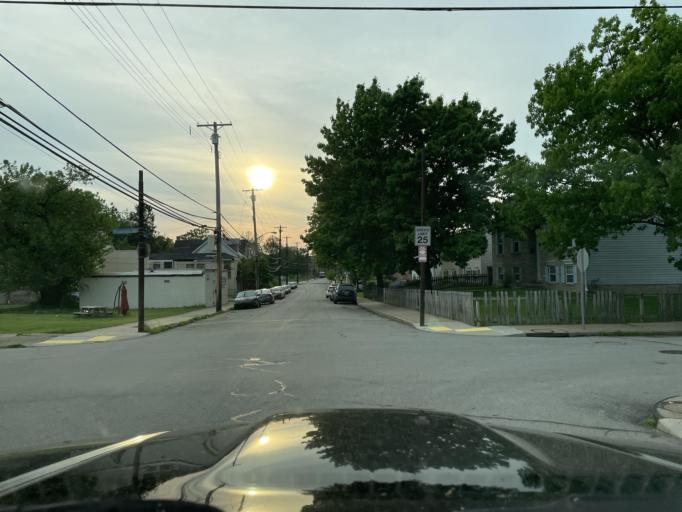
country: US
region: Pennsylvania
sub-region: Allegheny County
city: Wilkinsburg
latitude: 40.4500
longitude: -79.8867
